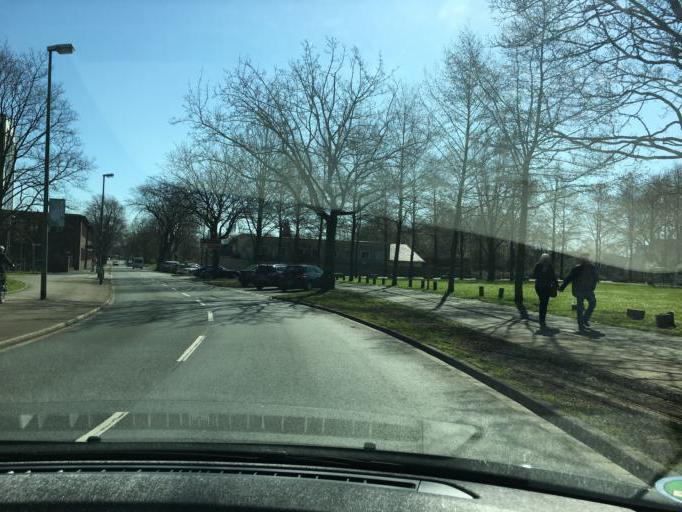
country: DE
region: North Rhine-Westphalia
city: Meiderich
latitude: 51.4593
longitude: 6.7289
